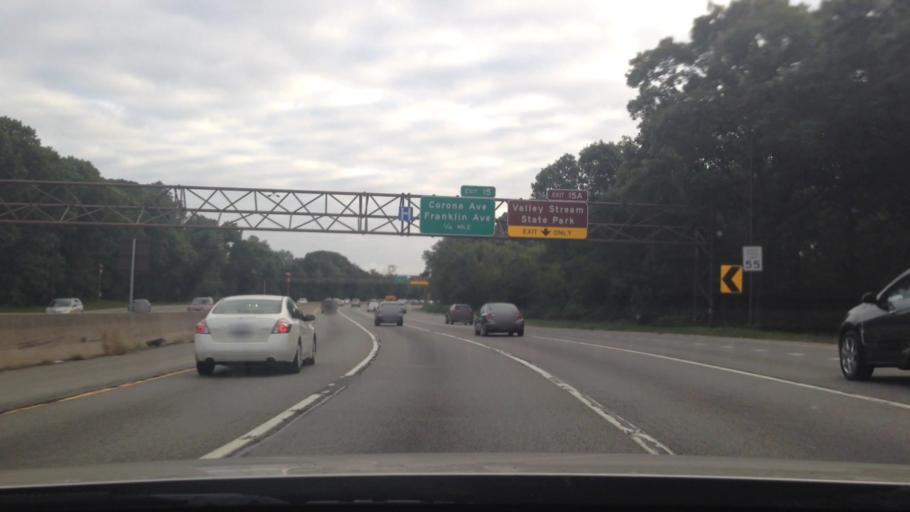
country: US
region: New York
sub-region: Nassau County
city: North Valley Stream
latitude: 40.6795
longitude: -73.6968
